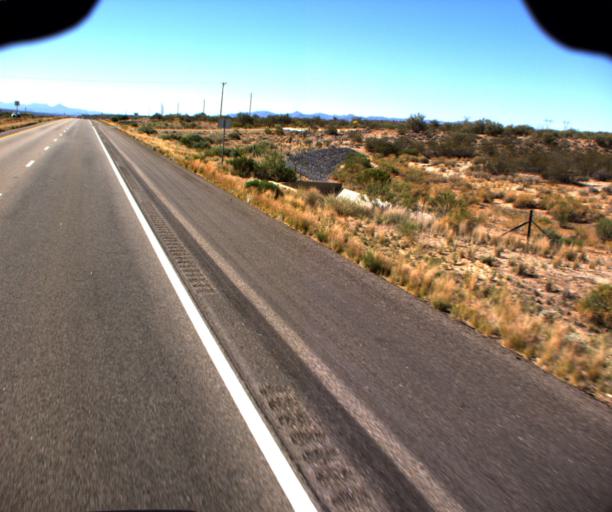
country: US
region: Arizona
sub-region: Mohave County
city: Kingman
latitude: 34.8543
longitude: -113.6393
